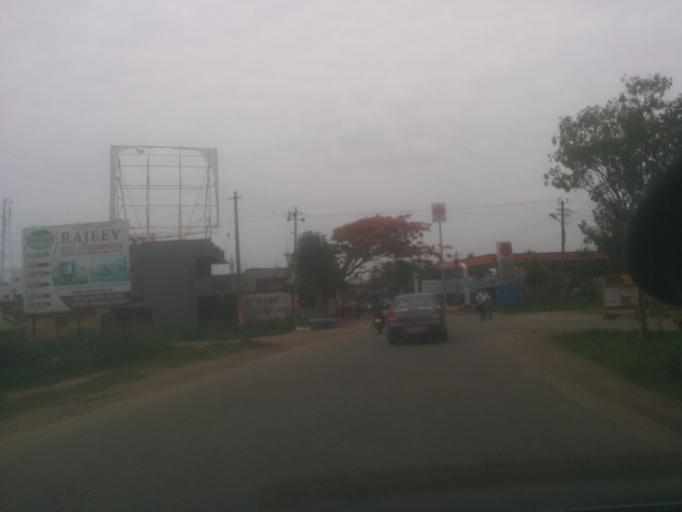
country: IN
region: Karnataka
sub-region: Hassan
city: Belur
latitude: 13.1694
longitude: 75.8735
